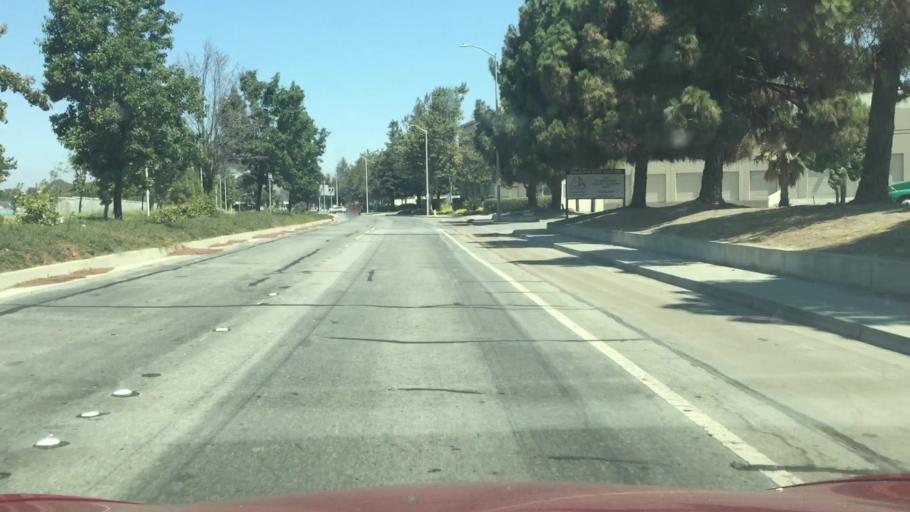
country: US
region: California
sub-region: Alameda County
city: Fremont
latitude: 37.5102
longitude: -121.9955
